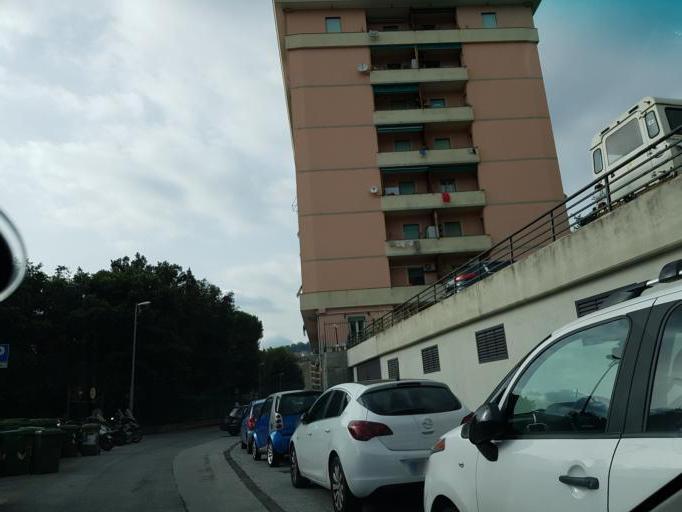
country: IT
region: Liguria
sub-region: Provincia di Genova
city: Genoa
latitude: 44.4462
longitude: 8.8961
